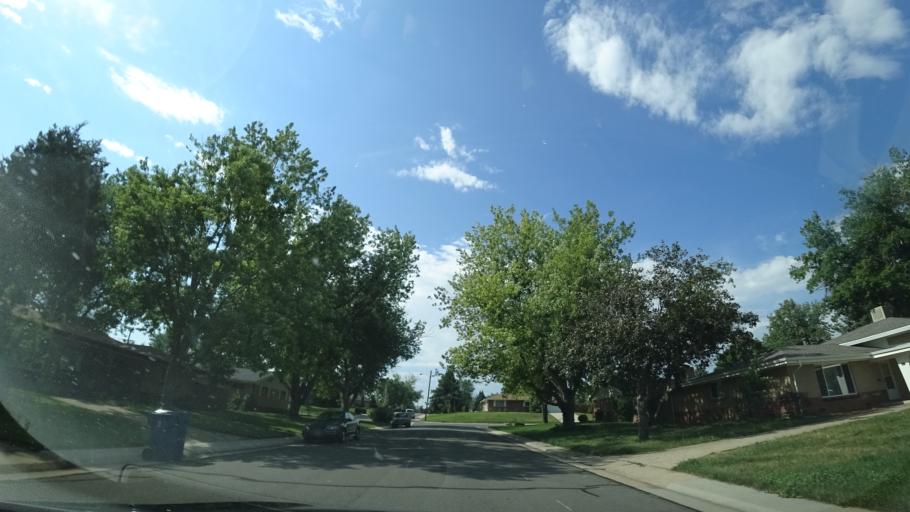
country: US
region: Colorado
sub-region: Jefferson County
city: Lakewood
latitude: 39.7137
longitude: -105.0571
